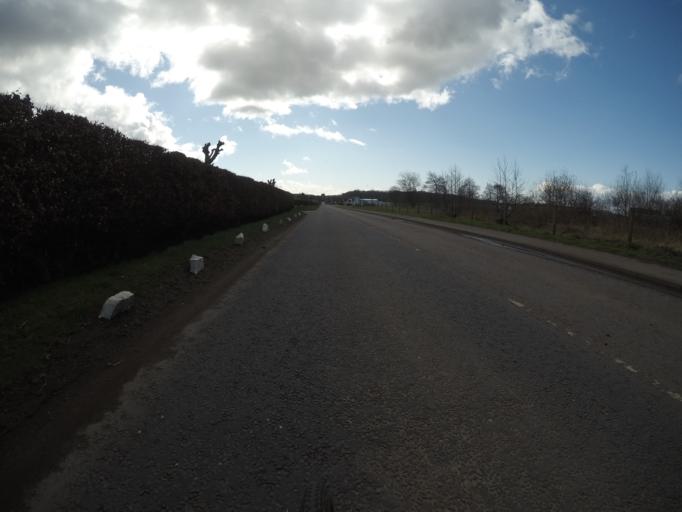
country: GB
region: Scotland
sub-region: North Ayrshire
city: Dreghorn
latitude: 55.5893
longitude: -4.6015
